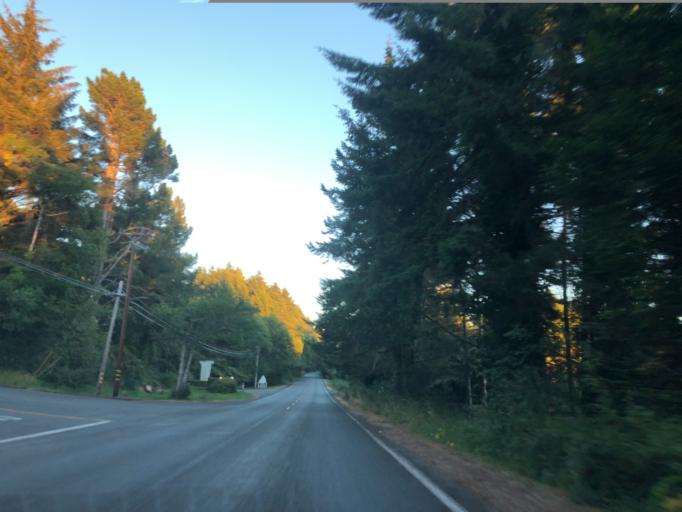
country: US
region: California
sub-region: Humboldt County
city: Westhaven-Moonstone
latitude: 41.0943
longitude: -124.1559
